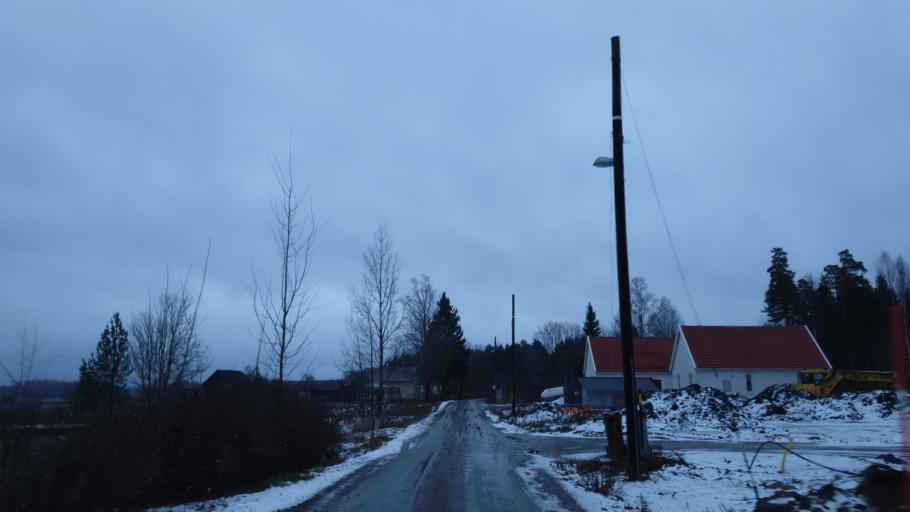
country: SE
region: Uppsala
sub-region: Tierps Kommun
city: Tierp
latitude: 60.3432
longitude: 17.4704
